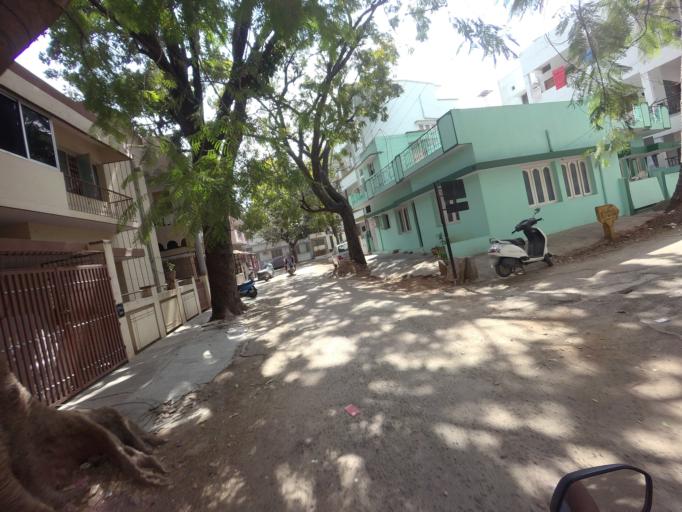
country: IN
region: Karnataka
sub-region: Bangalore Urban
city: Bangalore
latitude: 12.9626
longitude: 77.5367
